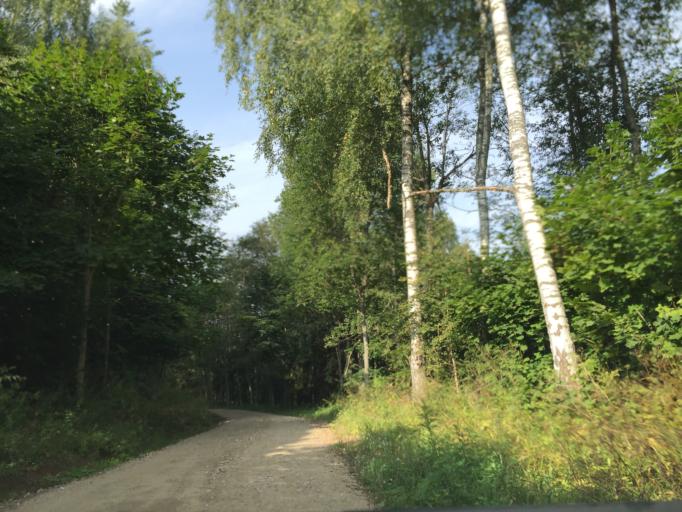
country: LV
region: Dagda
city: Dagda
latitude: 56.2662
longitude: 27.6500
